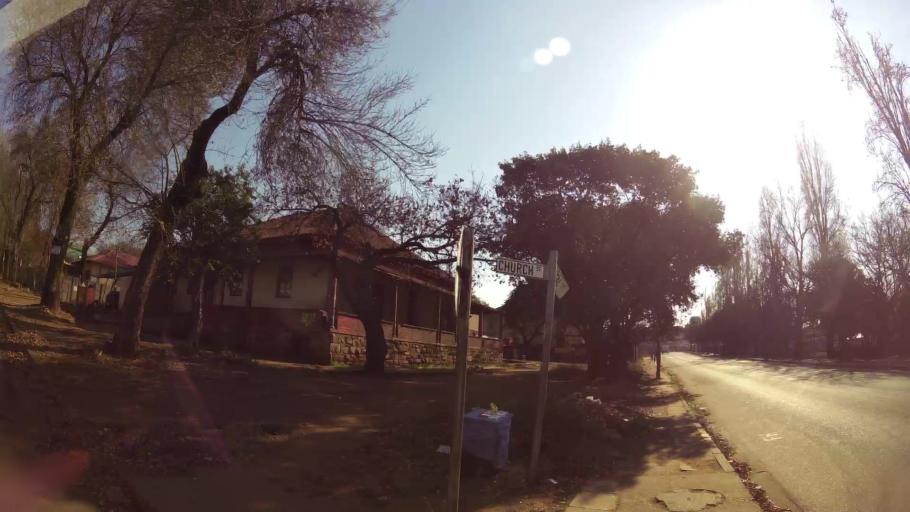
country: ZA
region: Gauteng
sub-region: Ekurhuleni Metropolitan Municipality
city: Boksburg
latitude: -26.2207
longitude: 28.2430
